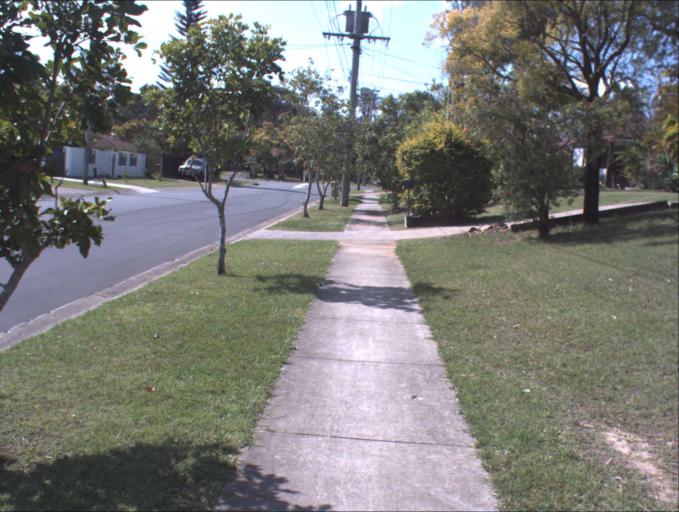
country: AU
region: Queensland
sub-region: Brisbane
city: Sunnybank Hills
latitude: -27.6640
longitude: 153.0536
